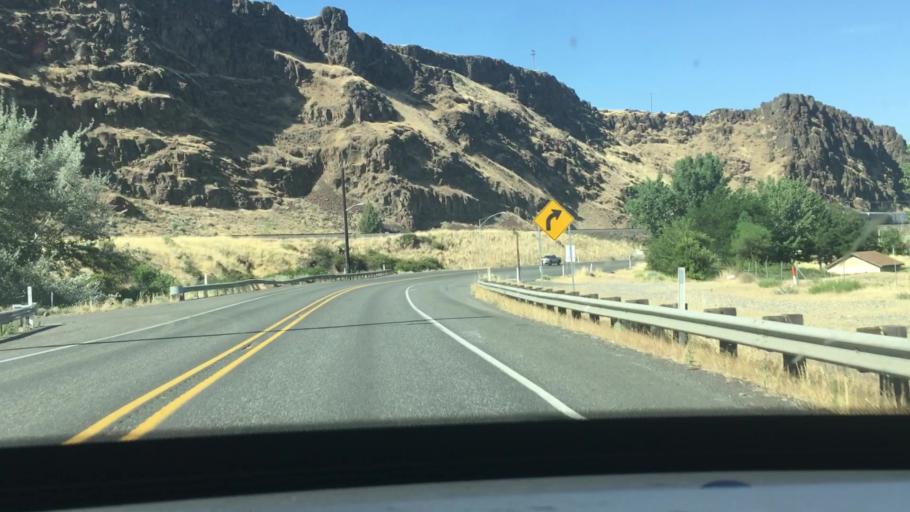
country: US
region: Washington
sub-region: Klickitat County
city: Goldendale
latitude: 45.6812
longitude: -120.8370
